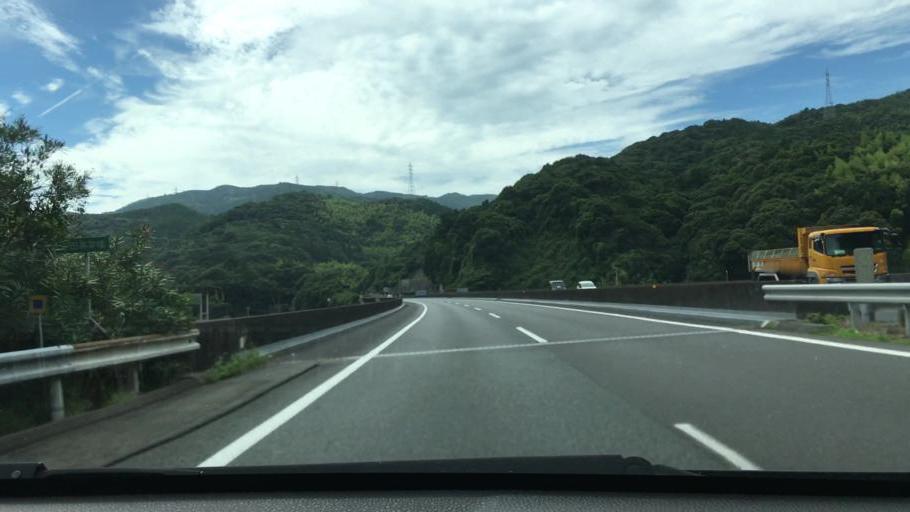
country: JP
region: Yamaguchi
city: Hofu
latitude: 34.0719
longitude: 131.6796
